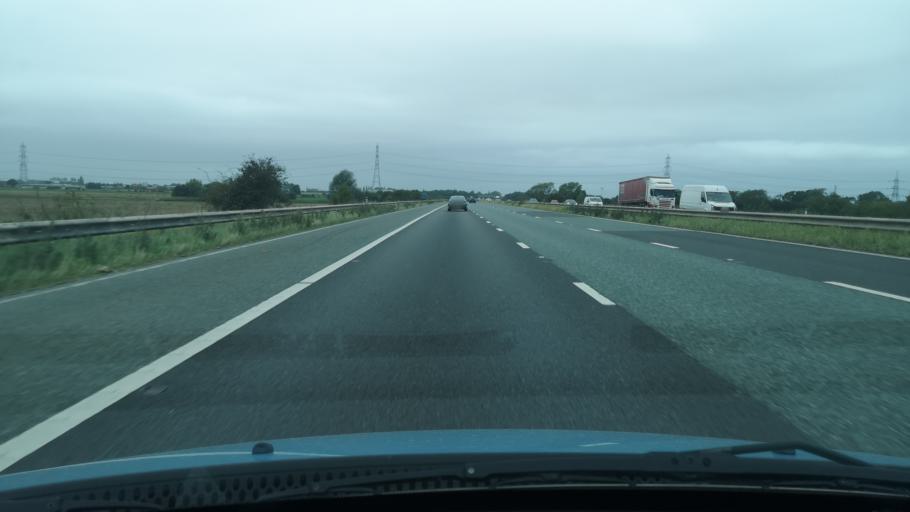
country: GB
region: England
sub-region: East Riding of Yorkshire
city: Snaith
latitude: 53.6796
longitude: -1.0376
